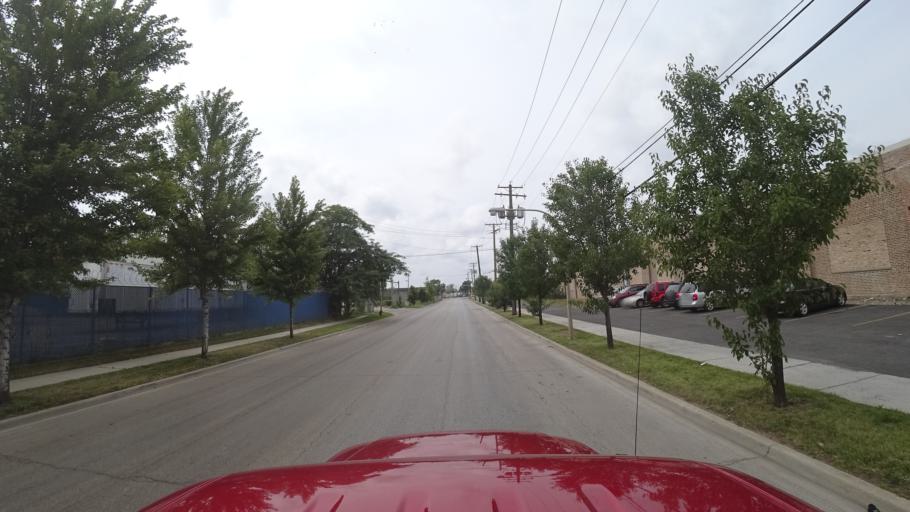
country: US
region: Illinois
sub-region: Cook County
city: Chicago
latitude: 41.8267
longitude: -87.6557
